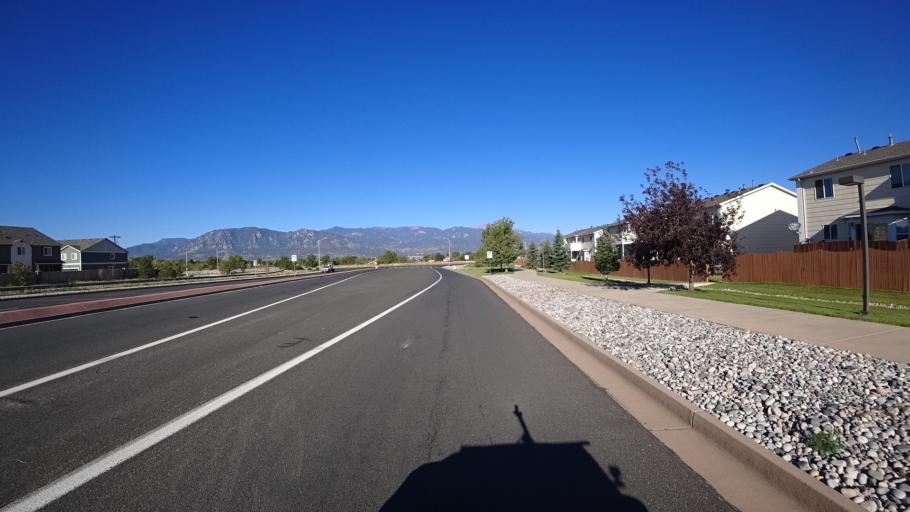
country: US
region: Colorado
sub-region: El Paso County
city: Stratmoor
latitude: 38.7891
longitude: -104.7375
